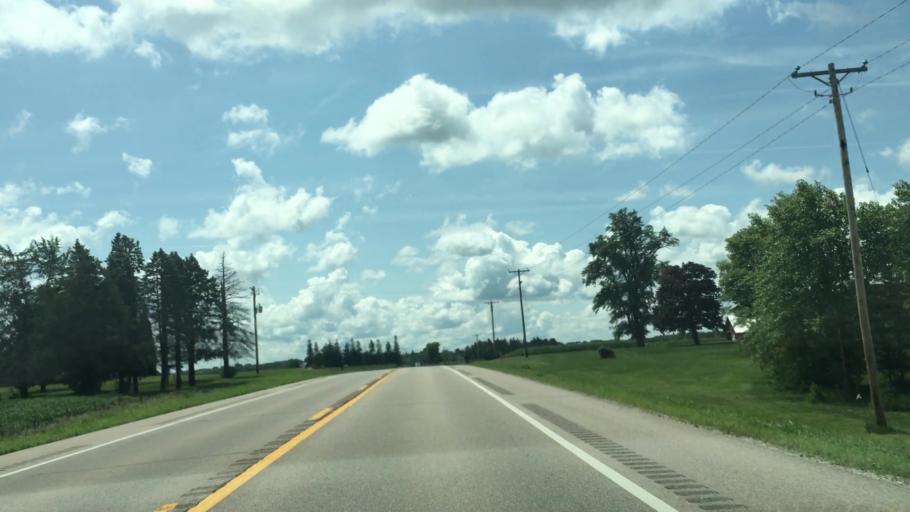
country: US
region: Iowa
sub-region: Johnson County
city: Solon
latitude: 41.8231
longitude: -91.4969
